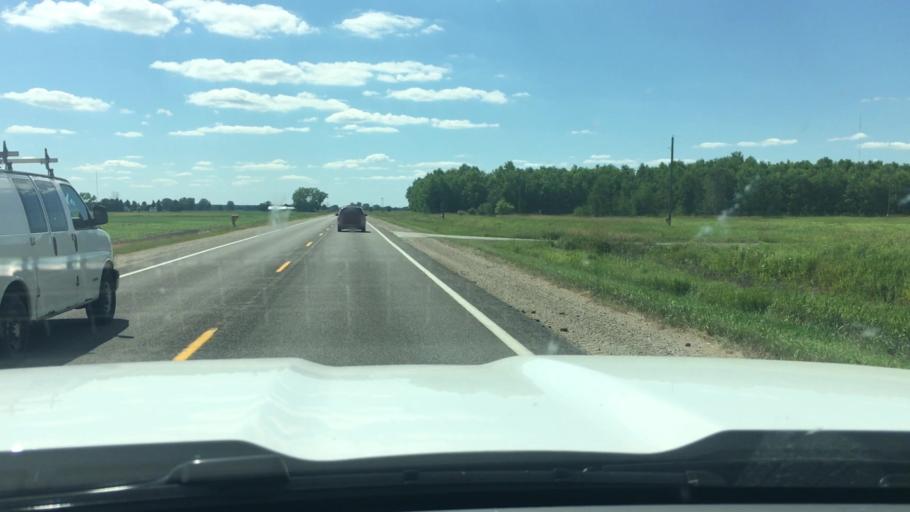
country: US
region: Michigan
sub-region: Clinton County
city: Ovid
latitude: 43.1759
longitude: -84.4358
